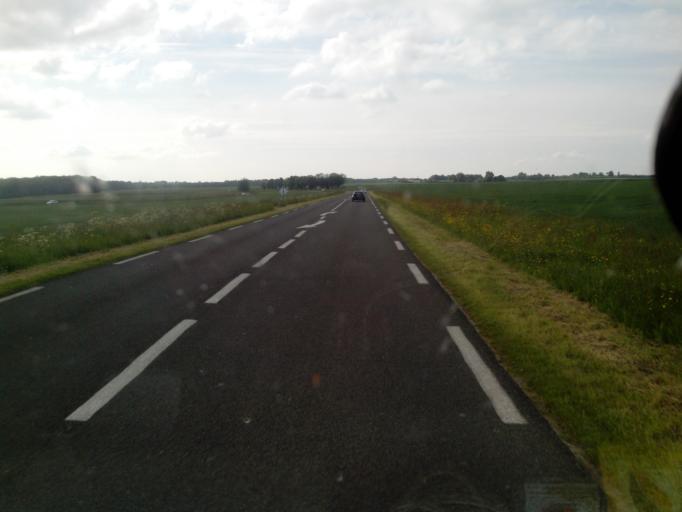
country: FR
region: Haute-Normandie
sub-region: Departement de la Seine-Maritime
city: Saint-Saens
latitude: 49.6564
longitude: 1.2596
